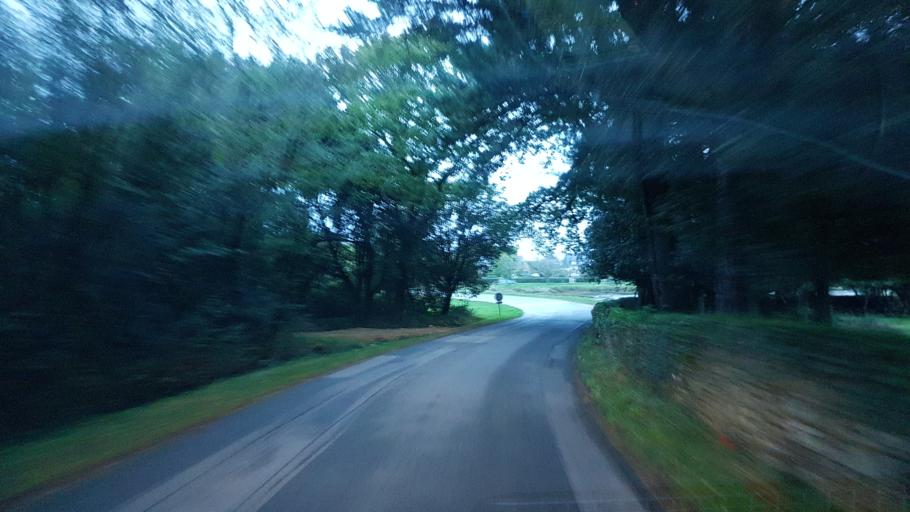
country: FR
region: Brittany
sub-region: Departement du Morbihan
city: Sarzeau
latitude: 47.5392
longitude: -2.7804
